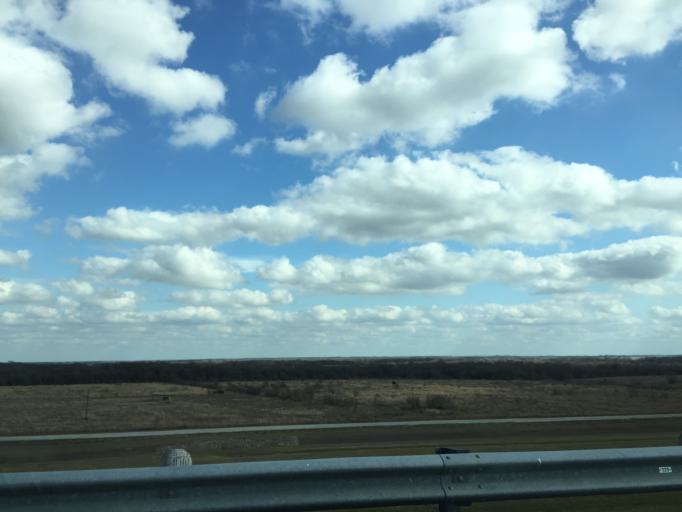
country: US
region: Texas
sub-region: Williamson County
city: Granger
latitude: 30.7119
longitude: -97.3248
